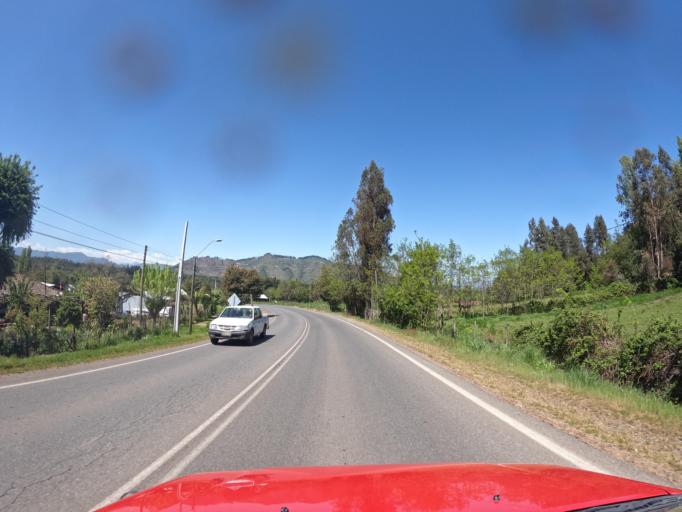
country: CL
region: Maule
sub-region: Provincia de Talca
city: San Clemente
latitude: -35.4897
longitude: -71.3006
